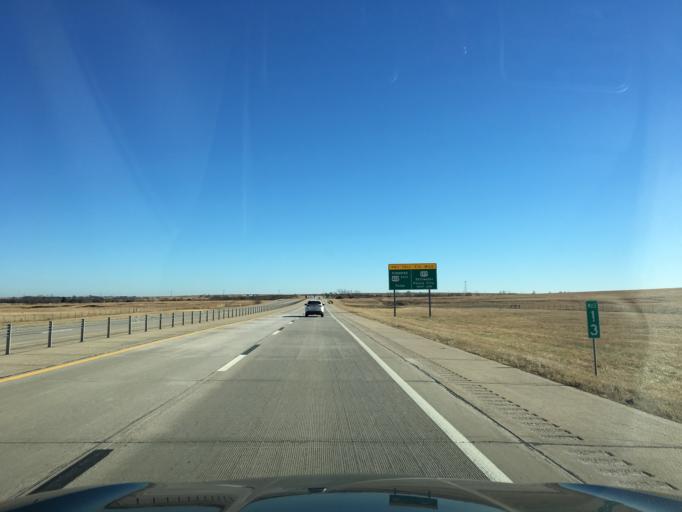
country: US
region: Oklahoma
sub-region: Noble County
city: Perry
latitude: 36.3895
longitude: -97.0959
